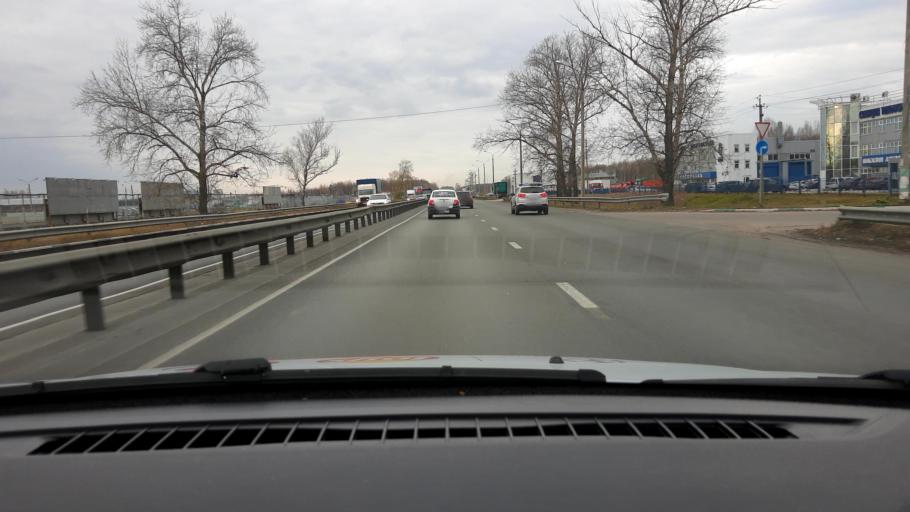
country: RU
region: Nizjnij Novgorod
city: Gorbatovka
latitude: 56.3091
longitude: 43.7946
